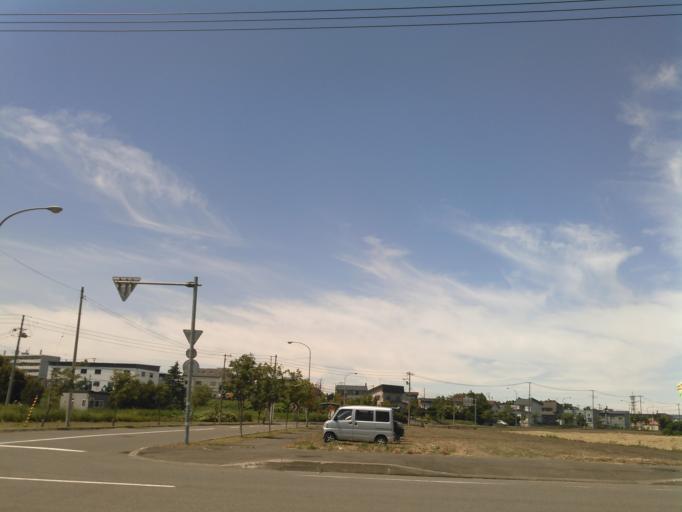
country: JP
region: Hokkaido
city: Ebetsu
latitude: 43.0975
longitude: 141.5542
